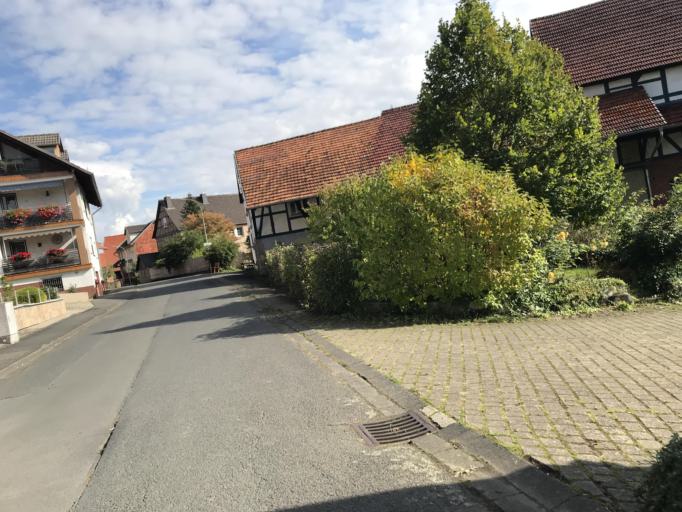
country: DE
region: Hesse
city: Felsberg
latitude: 51.1520
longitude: 9.4128
